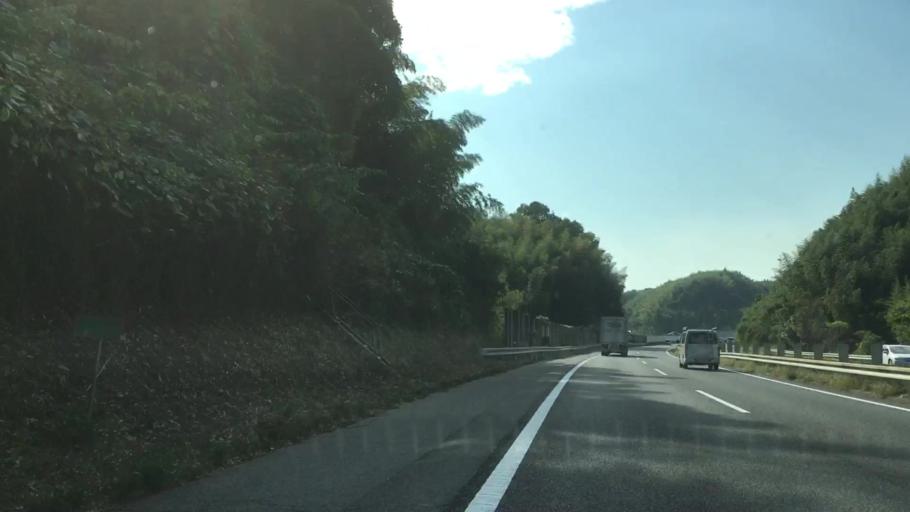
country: JP
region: Yamaguchi
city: Hikari
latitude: 34.0273
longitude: 131.9582
